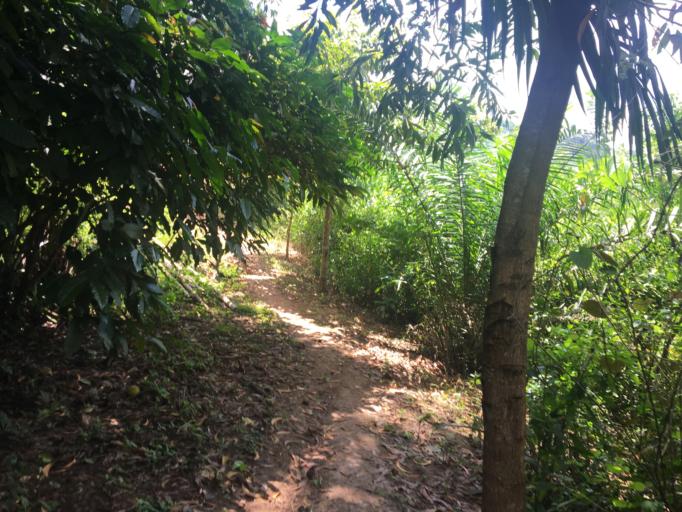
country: TG
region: Plateaux
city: Kpalime
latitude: 6.9595
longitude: 0.5396
